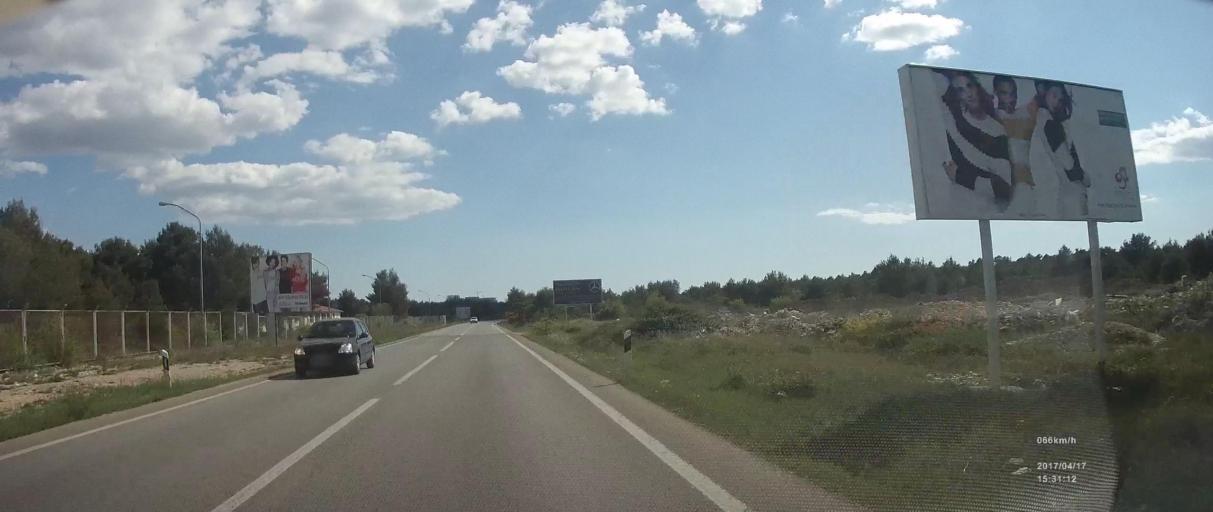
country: HR
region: Sibensko-Kniniska
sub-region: Grad Sibenik
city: Sibenik
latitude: 43.7041
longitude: 15.9073
